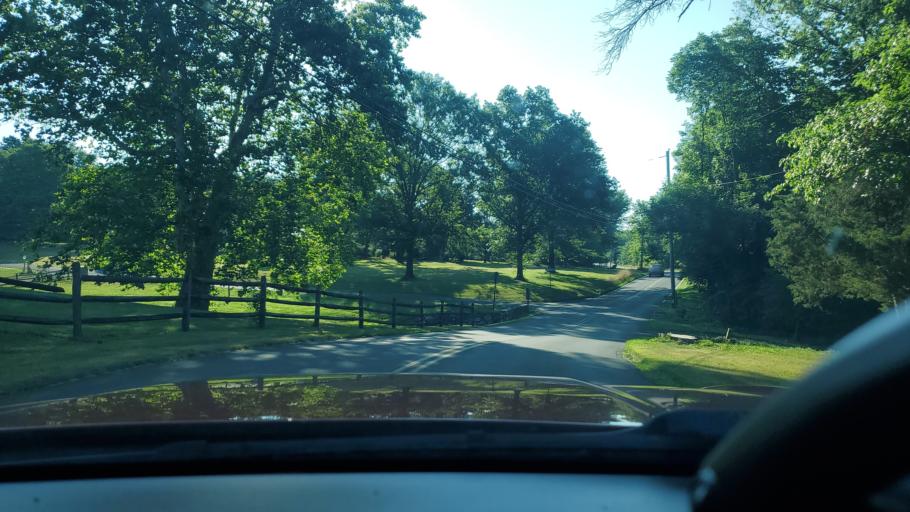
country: US
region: Pennsylvania
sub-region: Montgomery County
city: Harleysville
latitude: 40.2991
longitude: -75.3941
